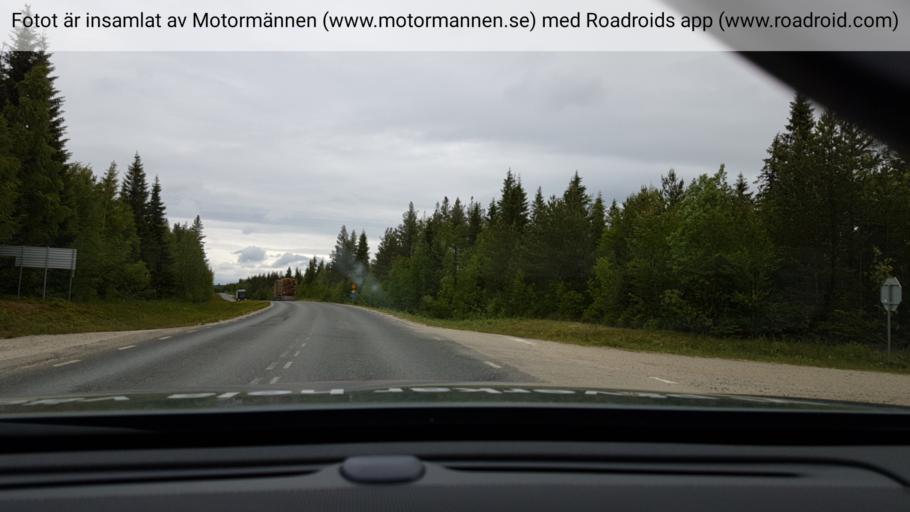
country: SE
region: Vaesterbotten
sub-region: Lycksele Kommun
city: Soderfors
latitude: 64.4860
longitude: 18.2764
